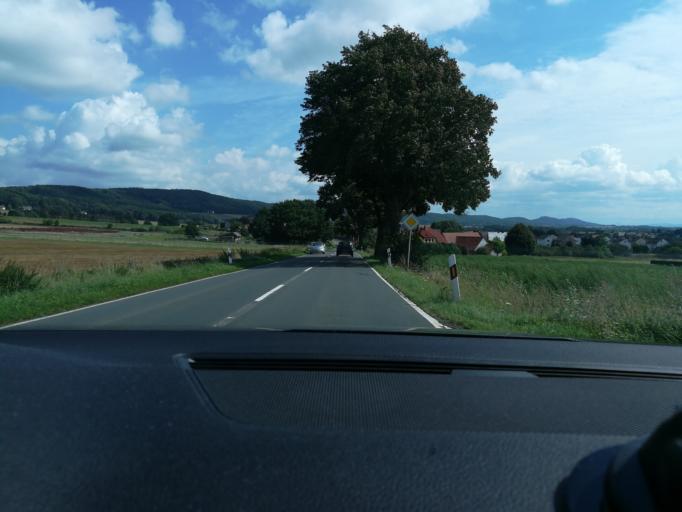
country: DE
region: North Rhine-Westphalia
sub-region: Regierungsbezirk Detmold
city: Huellhorst
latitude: 52.2873
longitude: 8.6498
